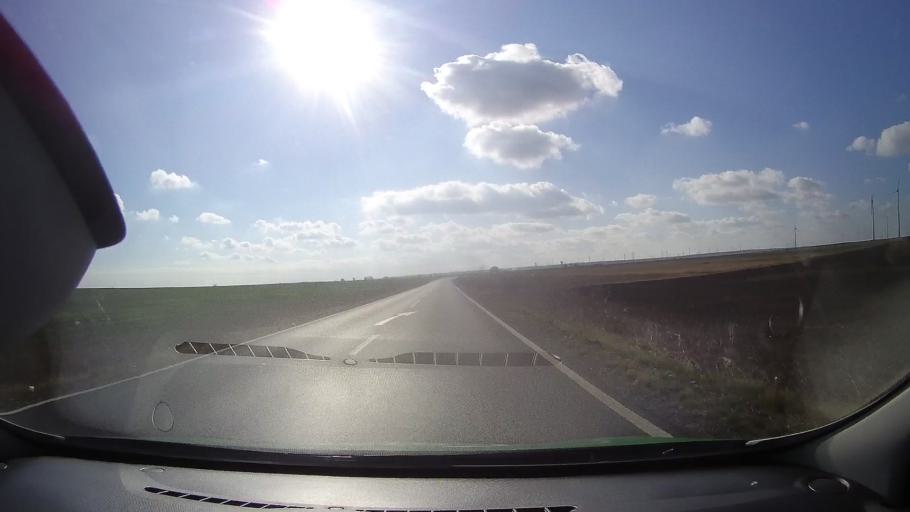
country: RO
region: Constanta
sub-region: Comuna Mihai Viteazu
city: Mihai Viteazu
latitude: 44.6696
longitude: 28.6834
